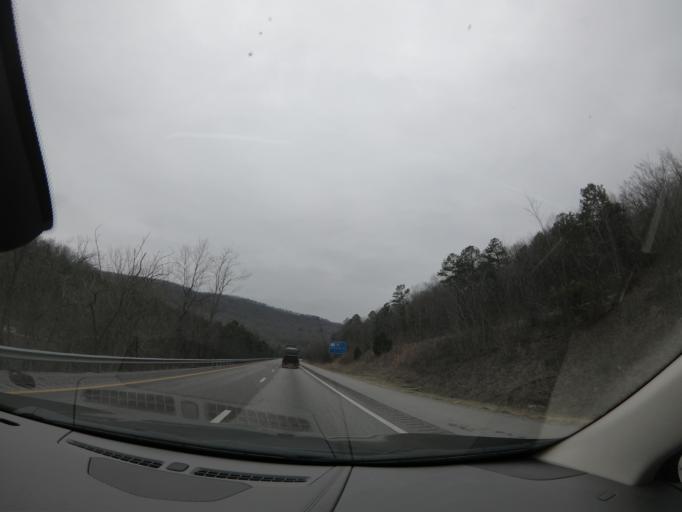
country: US
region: Tennessee
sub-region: Marion County
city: Jasper
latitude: 35.0065
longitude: -85.5202
